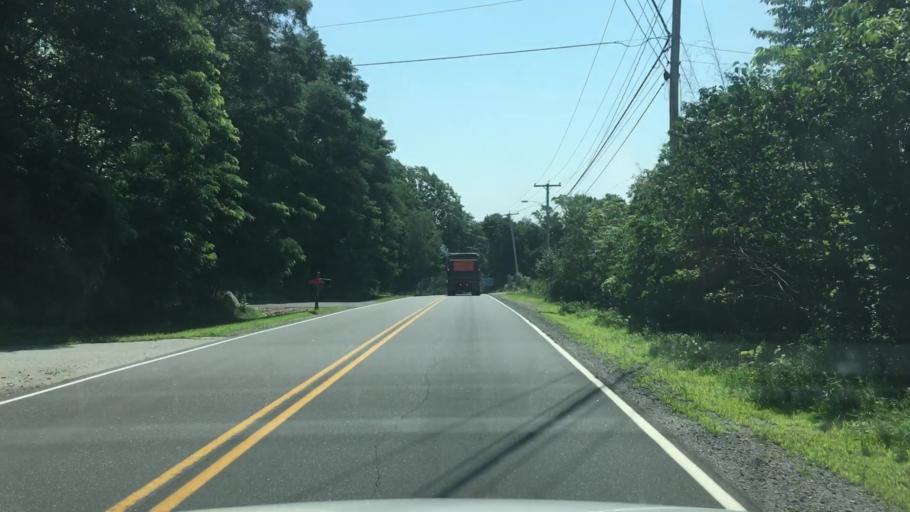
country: US
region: Maine
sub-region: Kennebec County
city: Hallowell
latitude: 44.3043
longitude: -69.8200
